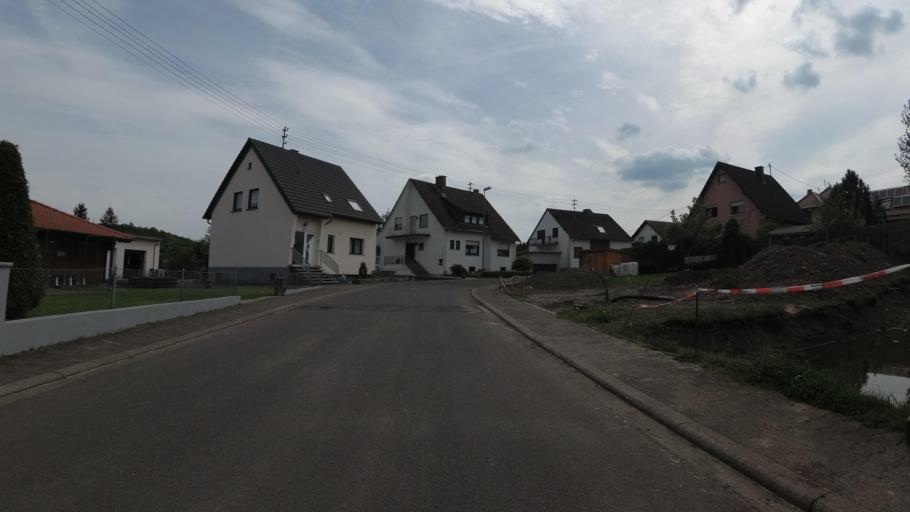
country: DE
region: Rheinland-Pfalz
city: Fohren-Linden
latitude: 49.5814
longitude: 7.2889
